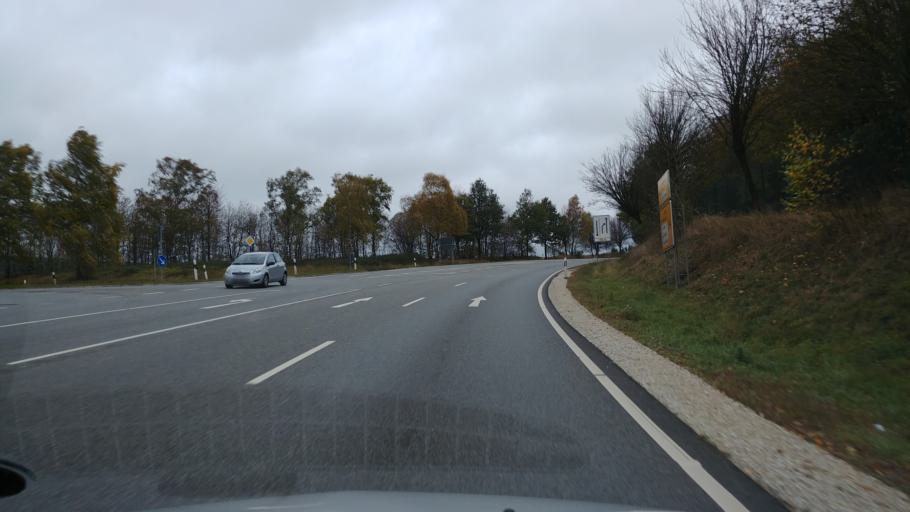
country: DE
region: Rheinland-Pfalz
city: Morbach
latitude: 49.7961
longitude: 7.1122
